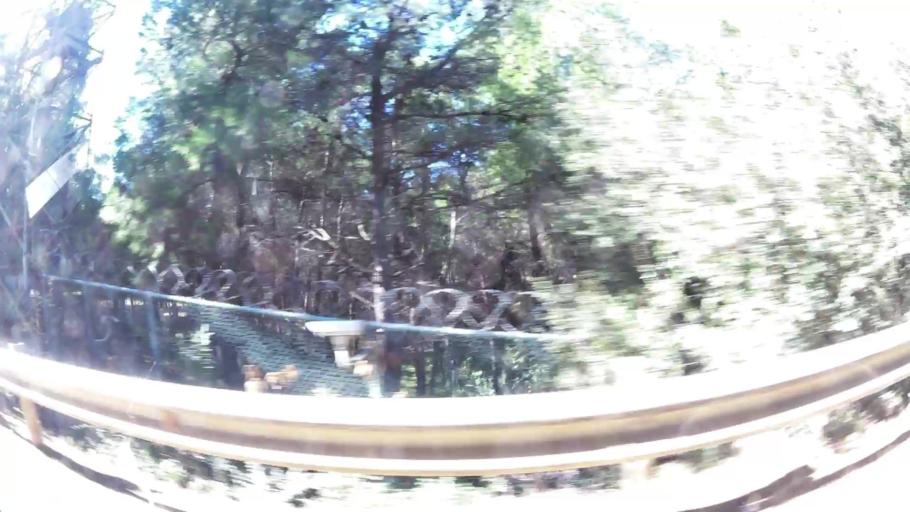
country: GR
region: Attica
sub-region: Nomarchia Anatolikis Attikis
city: Varybobi
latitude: 38.1181
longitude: 23.7993
